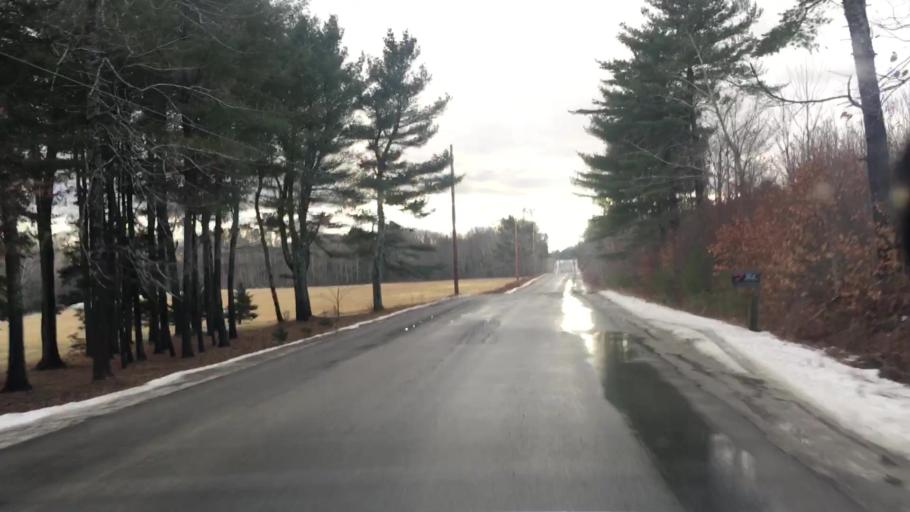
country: US
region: Maine
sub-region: Hancock County
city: Dedham
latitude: 44.6365
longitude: -68.7051
